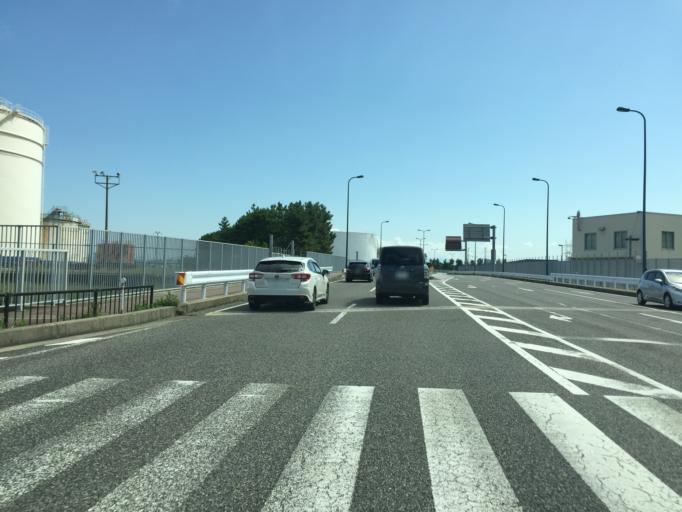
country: JP
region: Niigata
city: Niigata-shi
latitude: 37.9474
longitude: 139.0820
